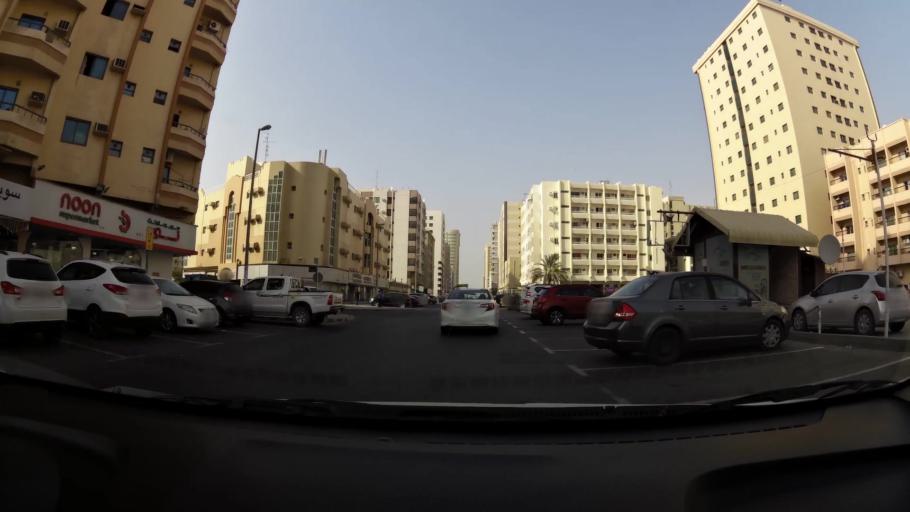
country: AE
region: Ash Shariqah
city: Sharjah
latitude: 25.3323
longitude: 55.3968
